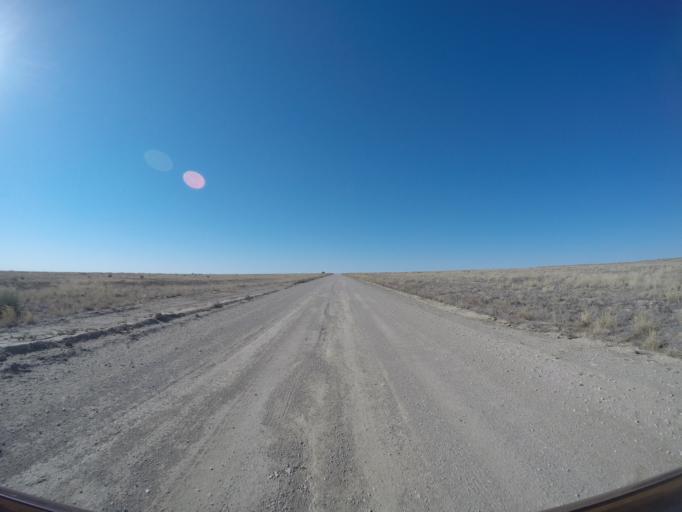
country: US
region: Colorado
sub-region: Otero County
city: La Junta
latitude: 37.7913
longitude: -103.5209
